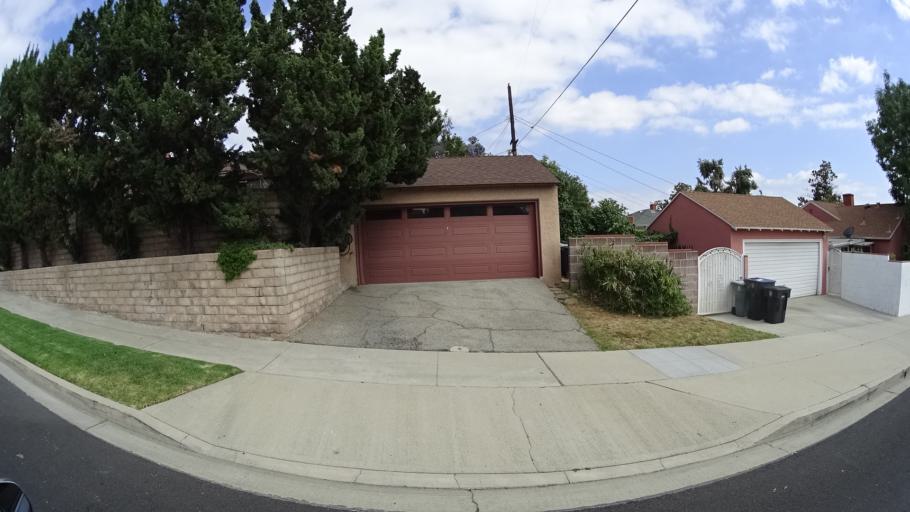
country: US
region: California
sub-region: Los Angeles County
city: Burbank
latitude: 34.2005
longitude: -118.3207
